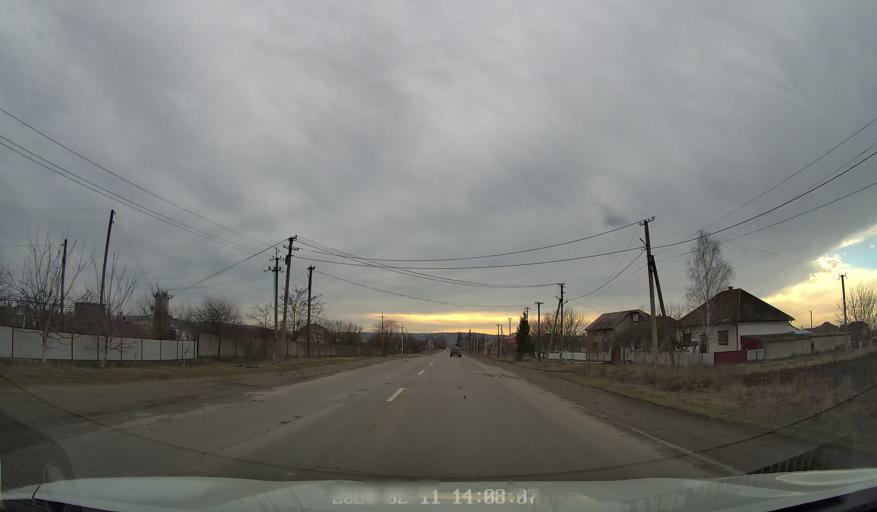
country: RO
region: Botosani
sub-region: Comuna Darabani
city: Bajura
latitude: 48.2405
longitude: 26.5479
